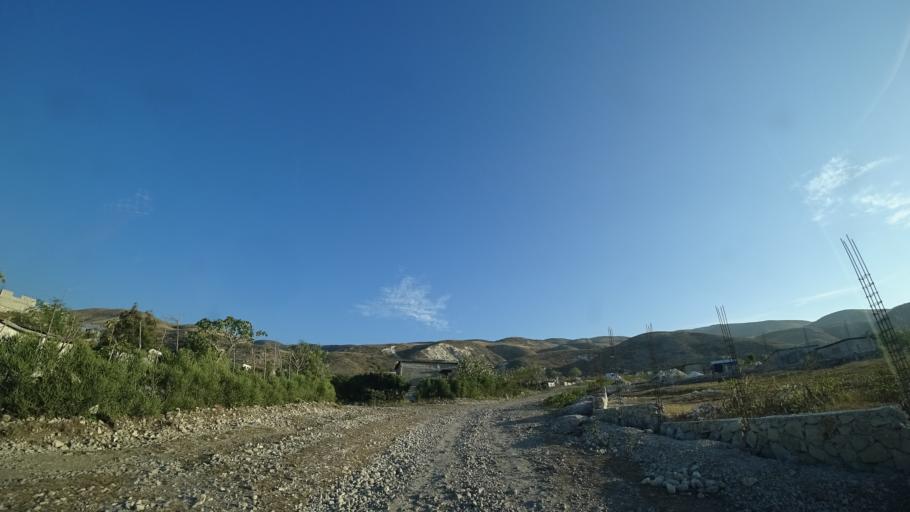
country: HT
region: Ouest
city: Cabaret
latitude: 18.6884
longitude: -72.3125
